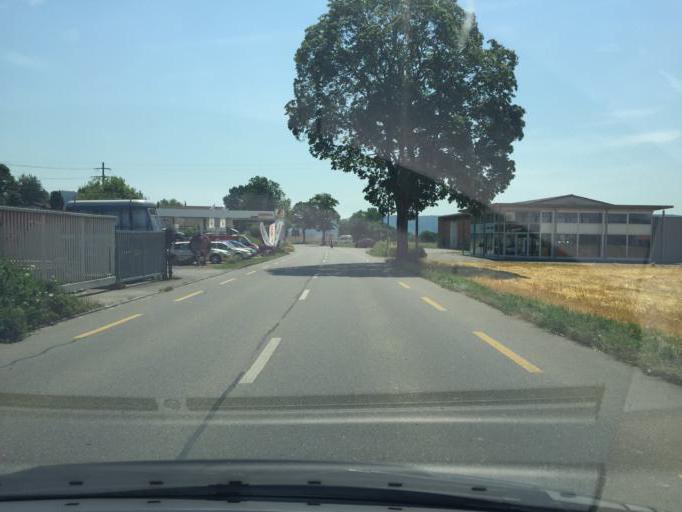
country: CH
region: Schaffhausen
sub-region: Bezirk Stein
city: Ramsen
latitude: 47.7055
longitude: 8.8202
